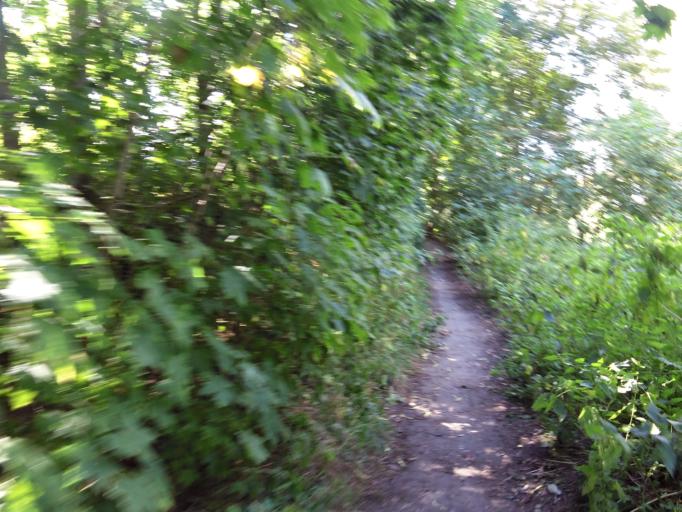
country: DE
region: Saxony
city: Leipzig
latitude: 51.3608
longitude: 12.4070
